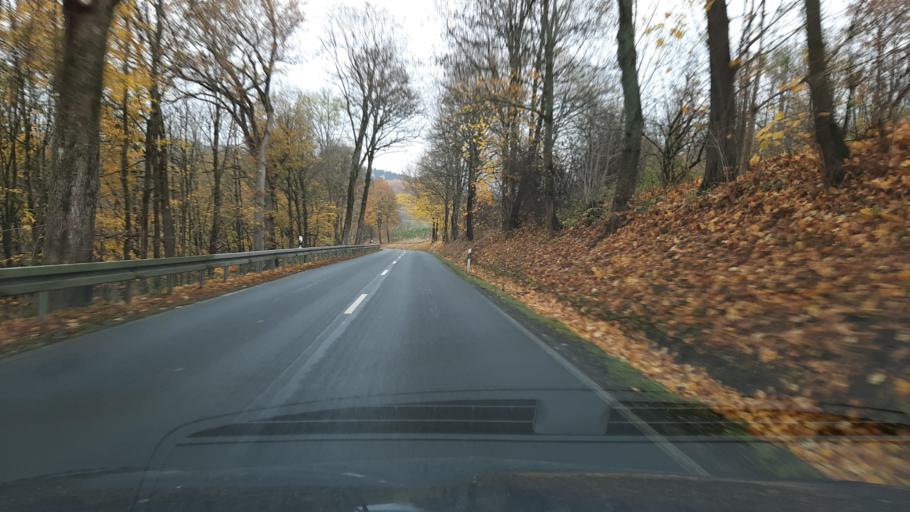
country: DE
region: North Rhine-Westphalia
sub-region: Regierungsbezirk Arnsberg
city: Winterberg
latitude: 51.2598
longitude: 8.4727
